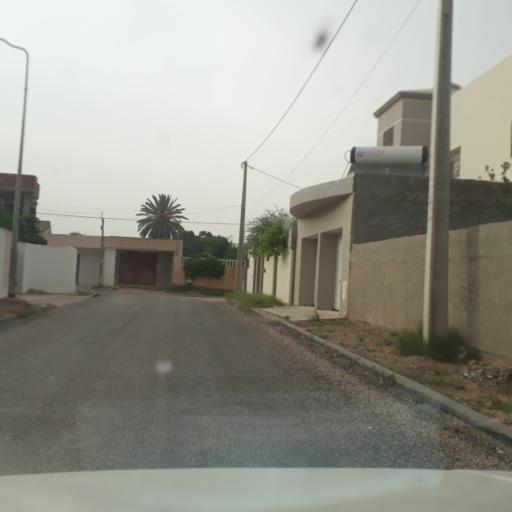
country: TN
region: Safaqis
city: Al Qarmadah
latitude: 34.8139
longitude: 10.7662
